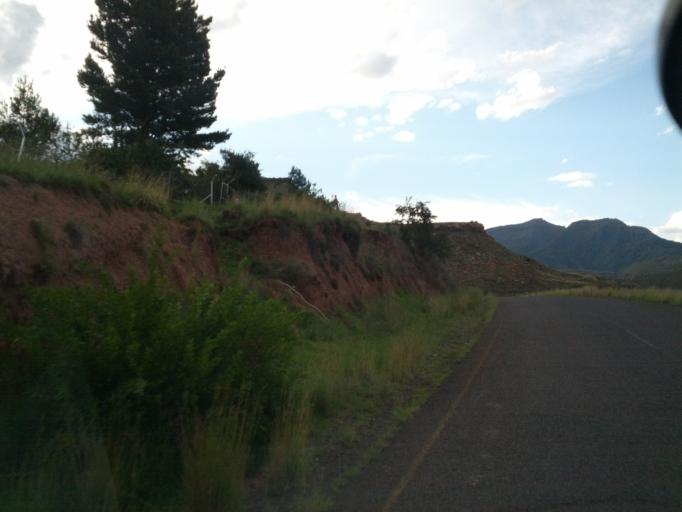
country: LS
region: Qacha's Nek
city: Qacha's Nek
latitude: -30.0664
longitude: 28.5326
